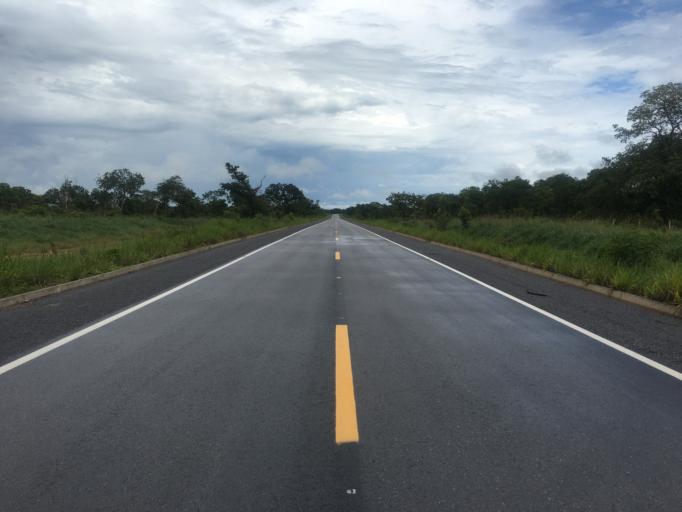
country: BR
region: Tocantins
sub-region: Taguatinga
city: Taguatinga
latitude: -12.4352
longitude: -46.8483
